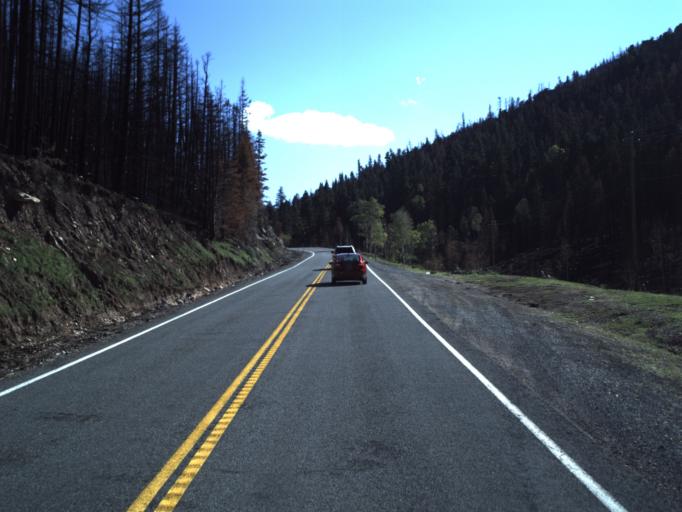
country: US
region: Utah
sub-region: Iron County
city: Parowan
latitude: 37.7408
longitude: -112.8379
